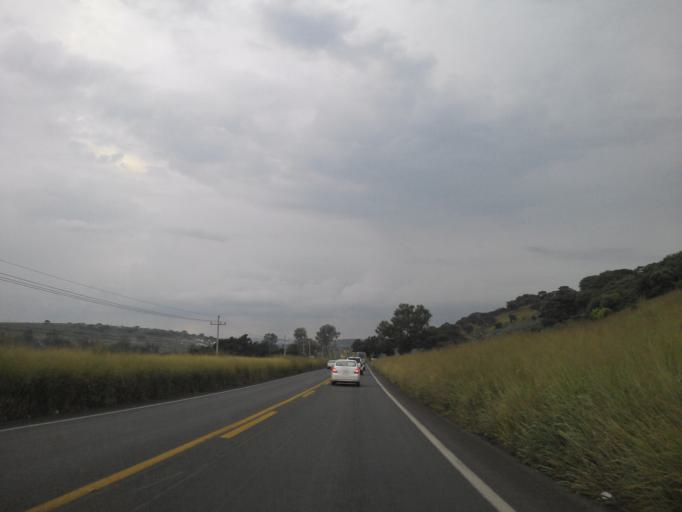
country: MX
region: Jalisco
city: Zapotlanejo
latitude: 20.6585
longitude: -103.0210
